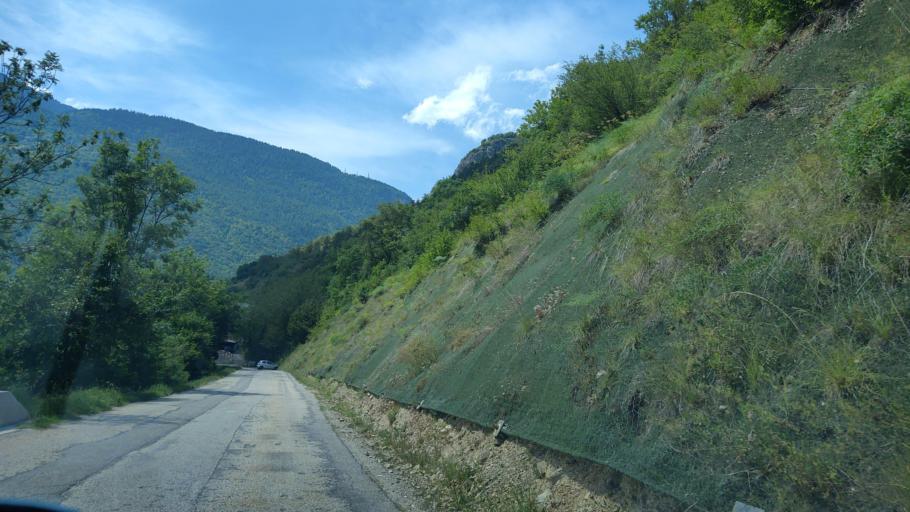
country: FR
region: Rhone-Alpes
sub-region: Departement de la Savoie
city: Salins-les-Thermes
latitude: 45.4651
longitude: 6.5438
